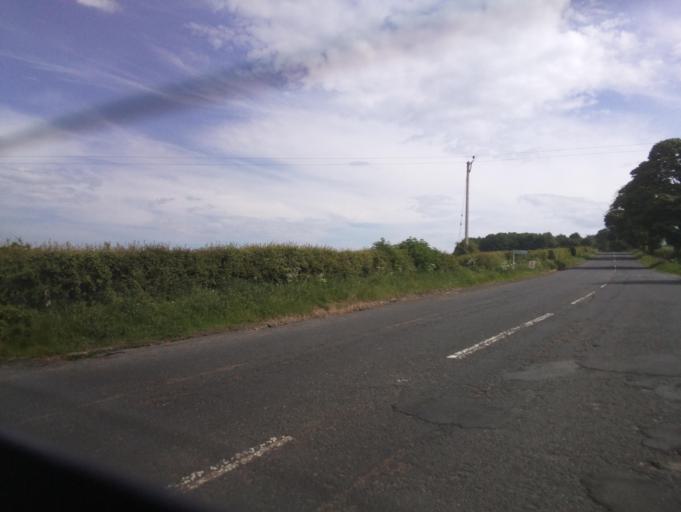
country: GB
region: England
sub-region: Northumberland
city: Alnwick
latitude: 55.4580
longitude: -1.7149
